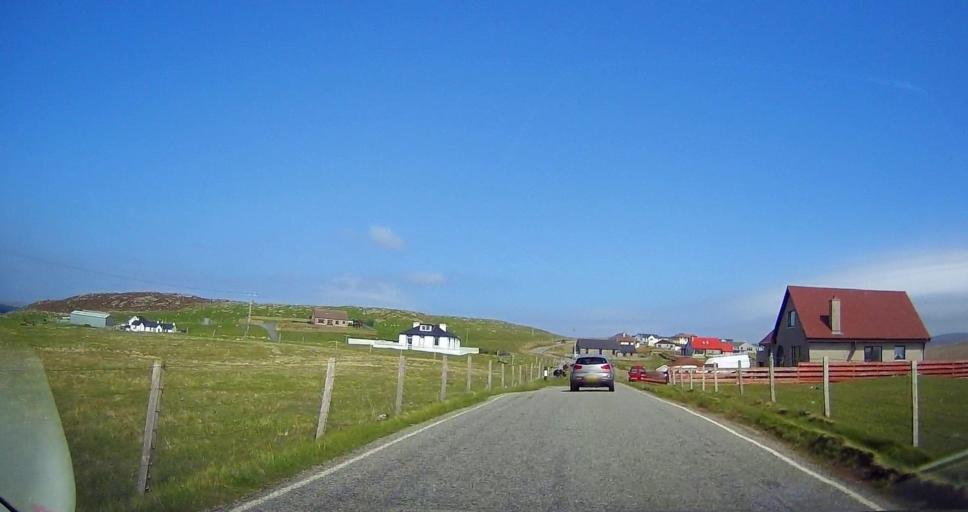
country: GB
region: Scotland
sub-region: Shetland Islands
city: Sandwick
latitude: 60.0844
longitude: -1.3321
